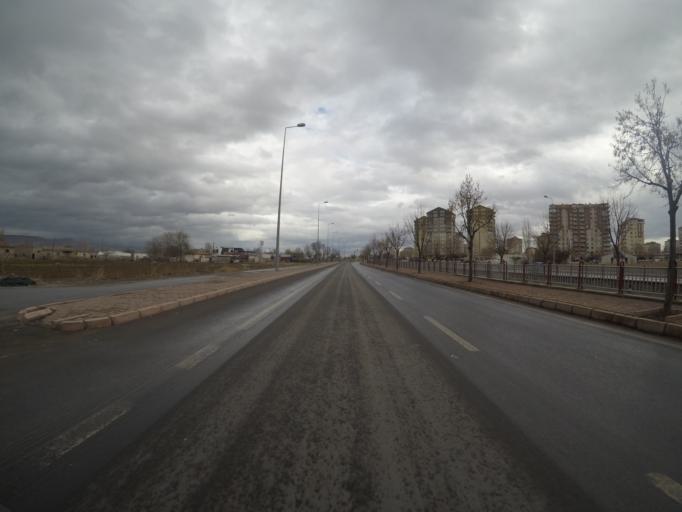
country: TR
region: Kayseri
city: Kayseri
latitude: 38.7572
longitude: 35.4807
